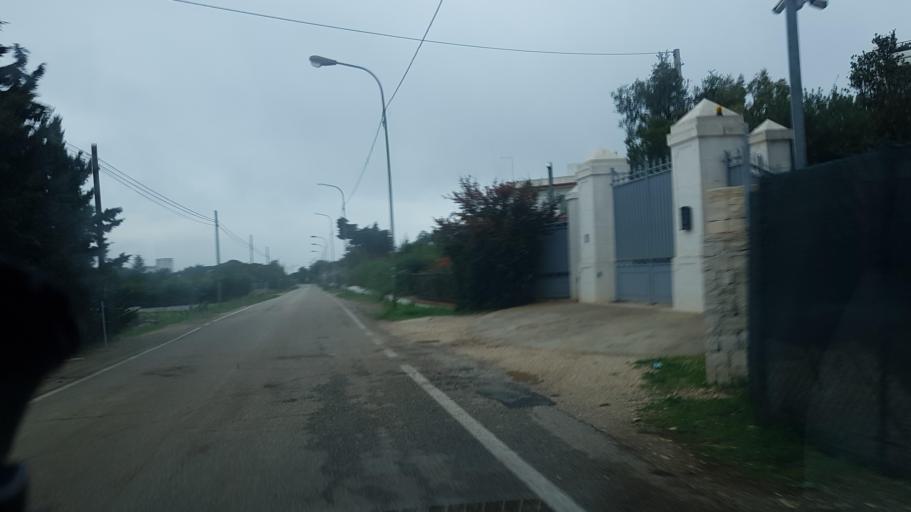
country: IT
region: Apulia
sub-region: Provincia di Brindisi
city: Ostuni
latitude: 40.7362
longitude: 17.5517
